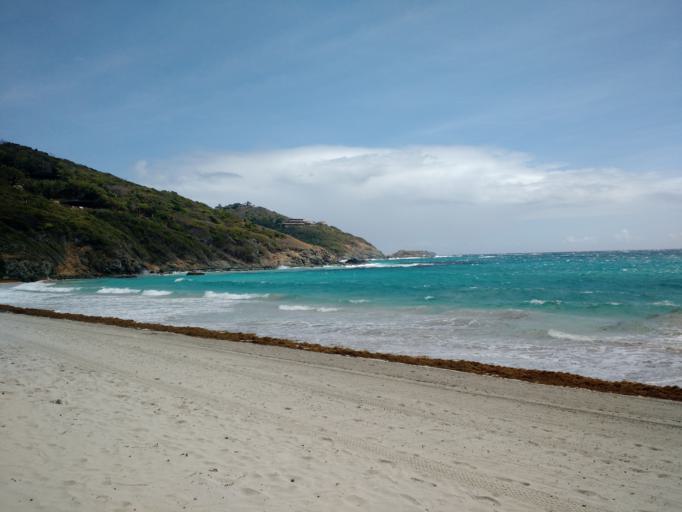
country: VC
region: Grenadines
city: Port Elizabeth
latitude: 12.8801
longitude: -61.1766
